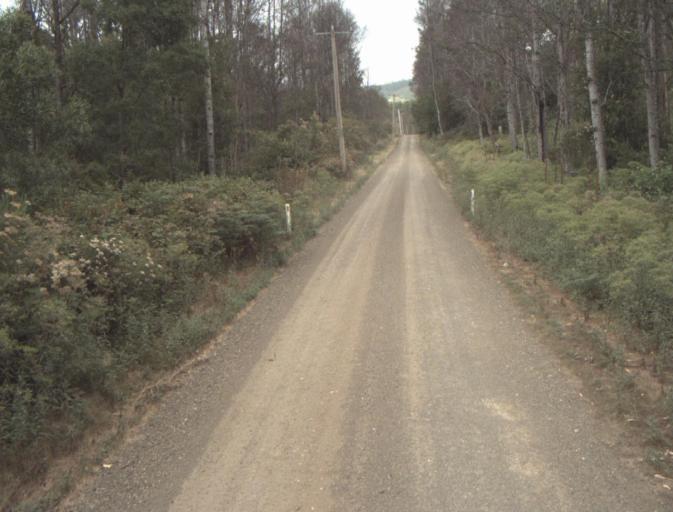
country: AU
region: Tasmania
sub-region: Dorset
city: Bridport
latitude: -41.1940
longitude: 147.2632
